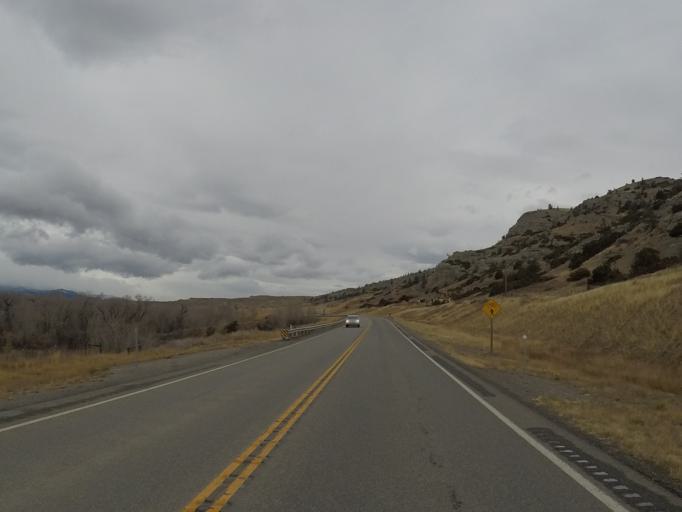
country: US
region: Montana
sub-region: Sweet Grass County
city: Big Timber
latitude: 45.8841
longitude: -109.9574
